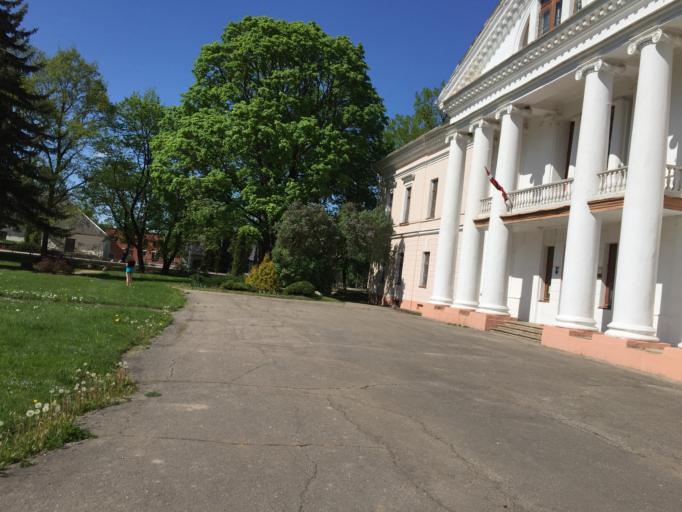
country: LV
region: Rundales
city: Pilsrundale
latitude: 56.3776
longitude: 23.9320
